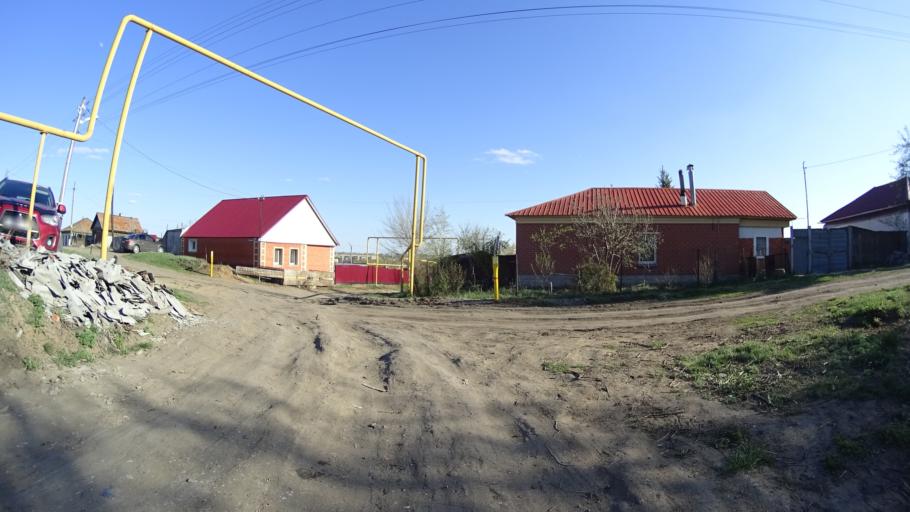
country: RU
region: Chelyabinsk
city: Troitsk
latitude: 54.0987
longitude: 61.5425
